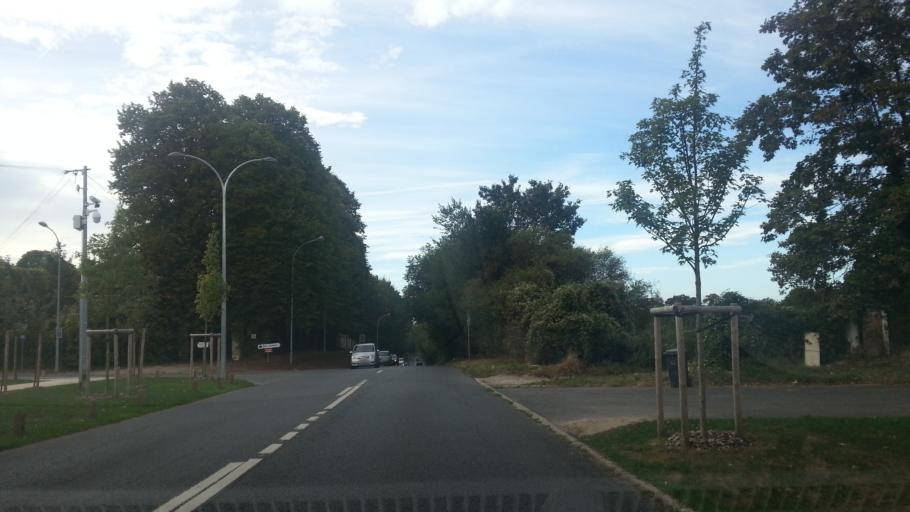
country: FR
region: Picardie
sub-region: Departement de l'Oise
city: Senlis
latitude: 49.2081
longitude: 2.5712
